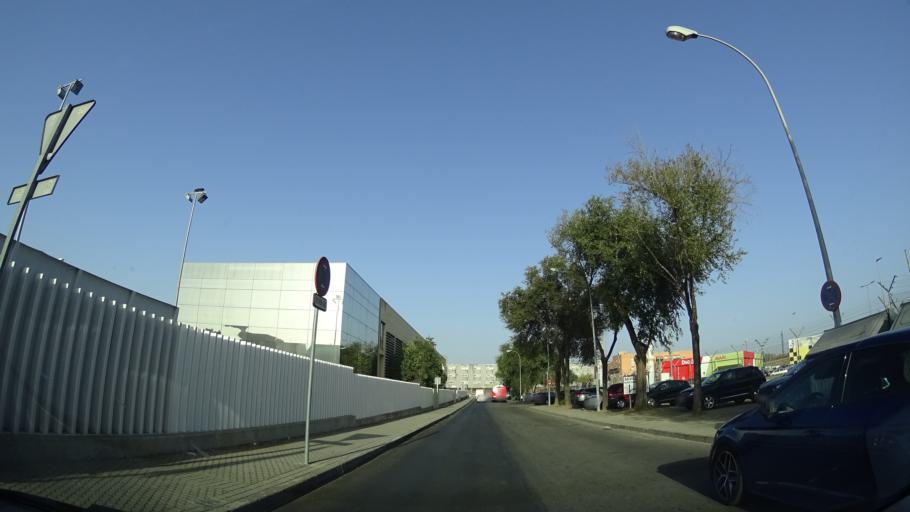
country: ES
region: Andalusia
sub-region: Provincia de Sevilla
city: La Algaba
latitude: 37.4312
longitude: -5.9782
